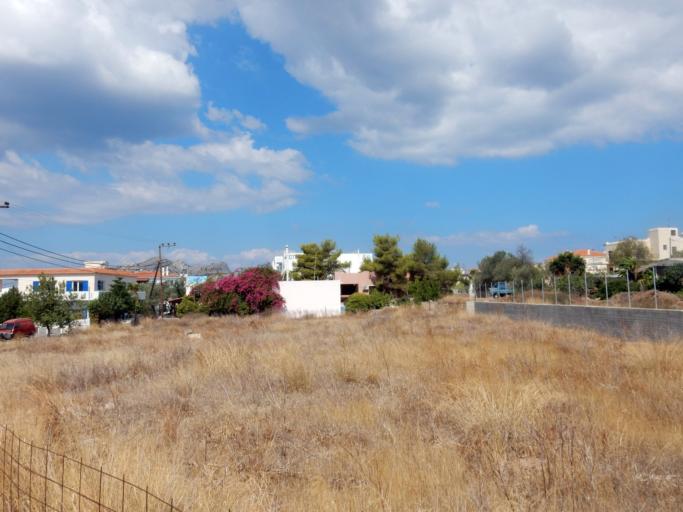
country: GR
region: Attica
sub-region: Nomos Piraios
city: Aegina
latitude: 37.6919
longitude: 23.4589
